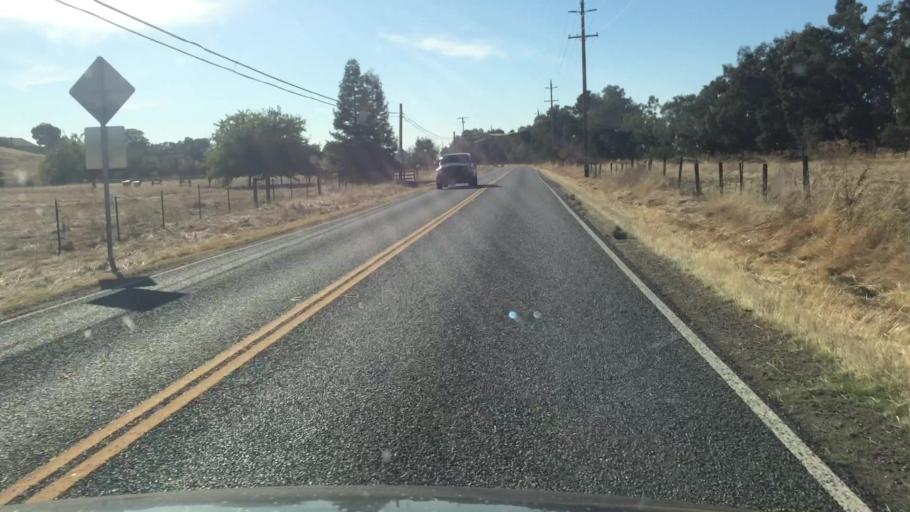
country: US
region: California
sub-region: Sacramento County
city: Clay
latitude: 38.3359
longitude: -121.1615
